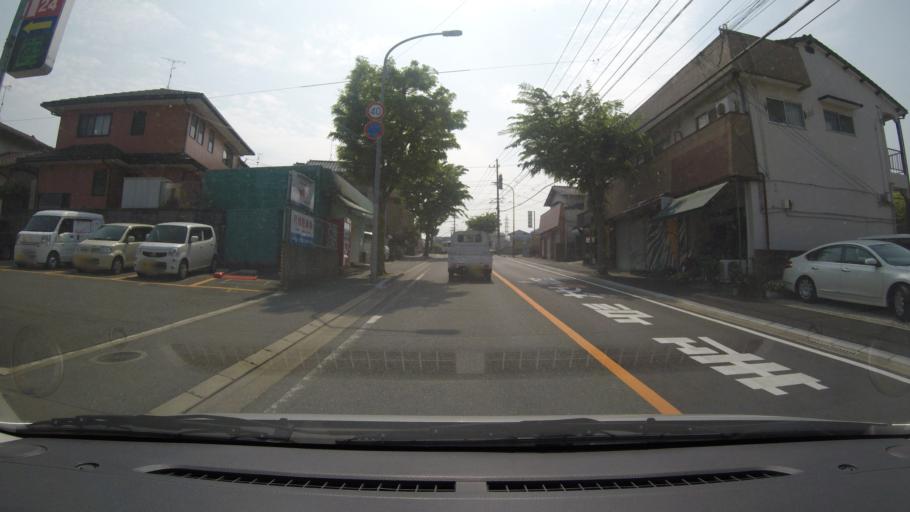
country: JP
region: Fukuoka
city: Fukuoka-shi
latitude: 33.6416
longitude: 130.4434
